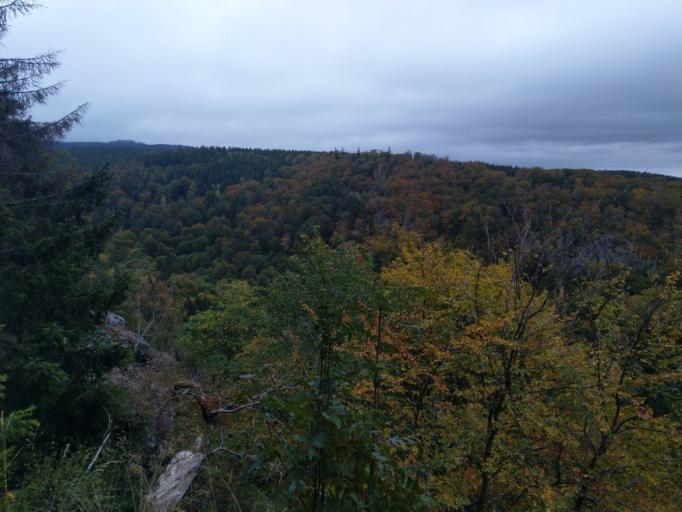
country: DE
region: Lower Saxony
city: Braunlage
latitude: 51.7504
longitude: 10.6751
